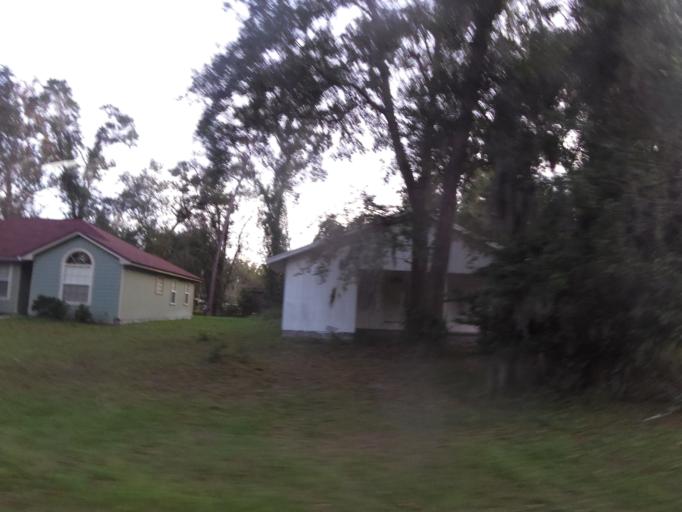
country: US
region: Florida
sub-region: Saint Johns County
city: Fruit Cove
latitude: 30.1612
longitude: -81.5424
